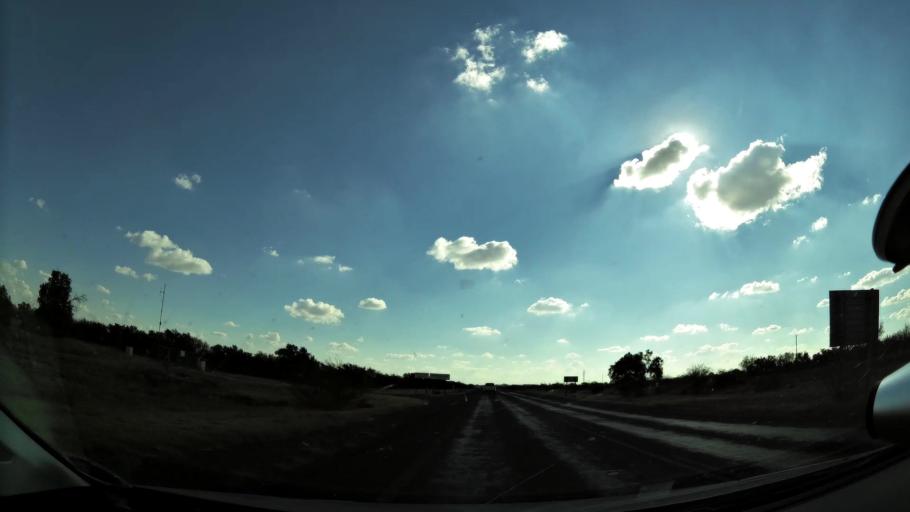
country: ZA
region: Northern Cape
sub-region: Frances Baard District Municipality
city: Kimberley
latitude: -28.8101
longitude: 24.8121
